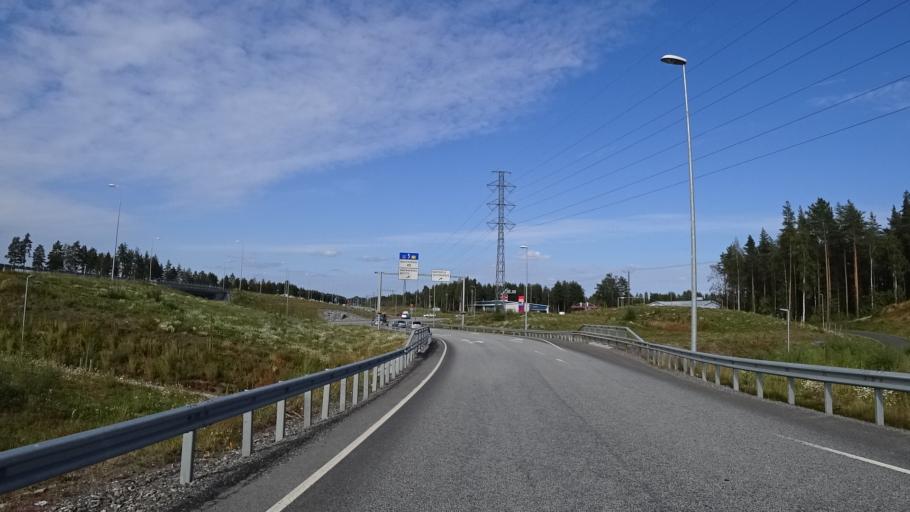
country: FI
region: North Karelia
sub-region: Joensuu
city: Joensuu
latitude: 62.6265
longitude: 29.7793
